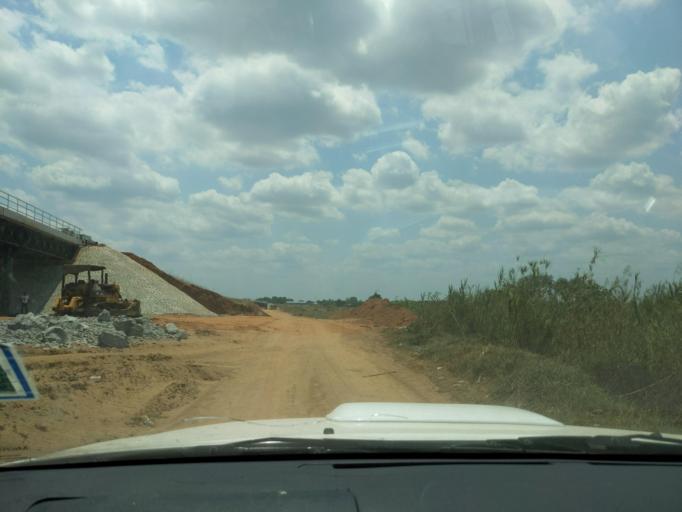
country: MZ
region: Zambezia
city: Quelimane
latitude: -17.2566
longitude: 37.0749
